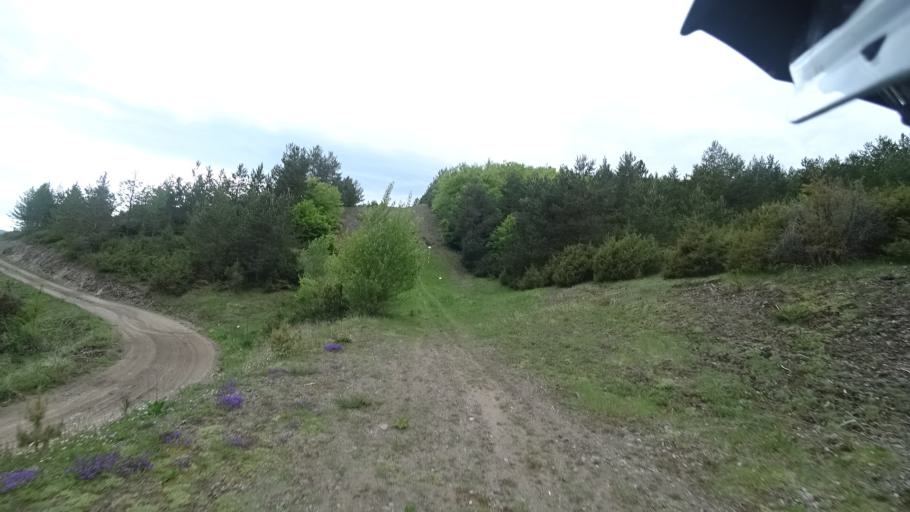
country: HR
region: Licko-Senjska
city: Jezerce
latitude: 44.8699
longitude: 15.4432
